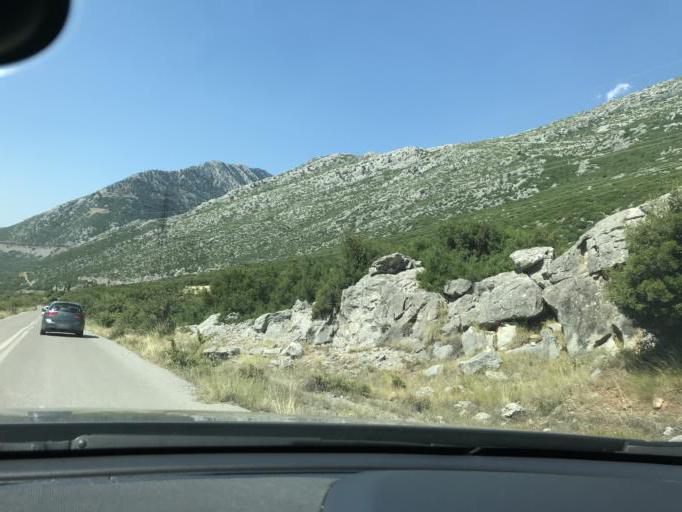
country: GR
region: Central Greece
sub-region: Nomos Voiotias
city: Distomo
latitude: 38.4909
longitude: 22.6931
